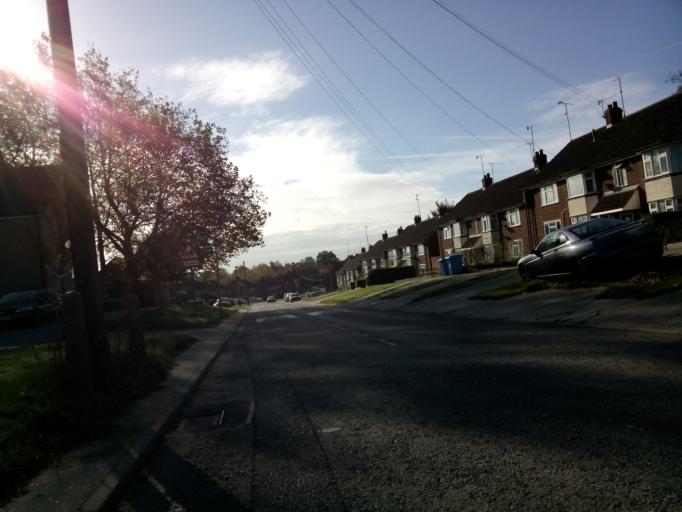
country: GB
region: England
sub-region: Suffolk
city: Ipswich
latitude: 52.0459
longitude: 1.1487
